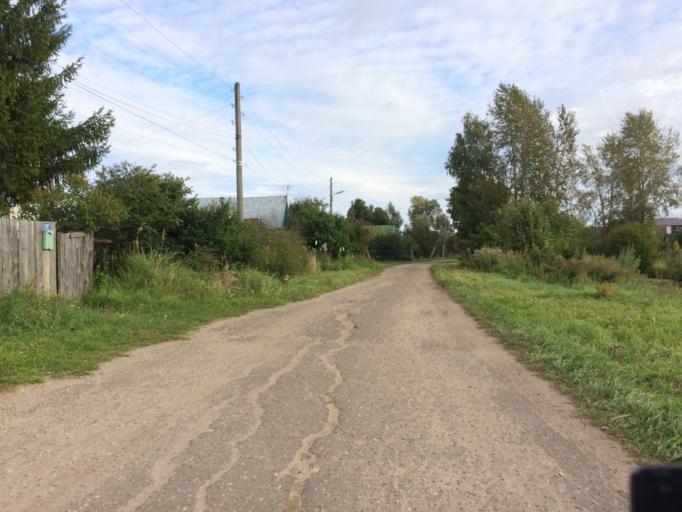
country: RU
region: Mariy-El
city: Yoshkar-Ola
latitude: 56.6536
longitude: 48.0139
